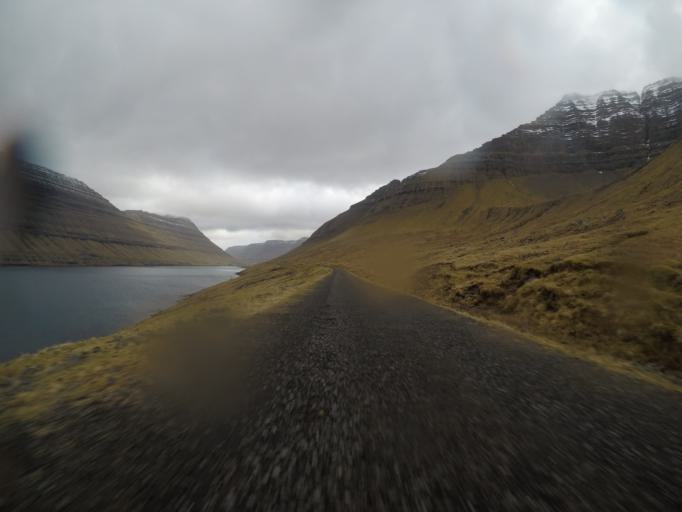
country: FO
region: Nordoyar
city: Klaksvik
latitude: 62.3203
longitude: -6.5591
